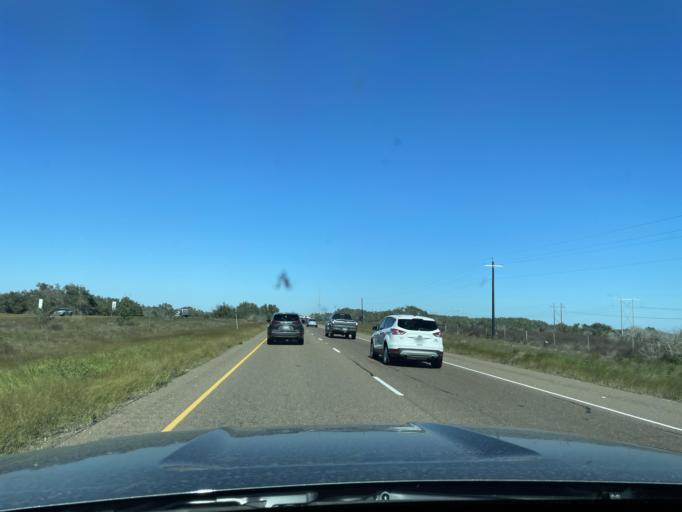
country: US
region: Texas
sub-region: Kenedy County
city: Sarita
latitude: 27.0092
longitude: -97.7944
